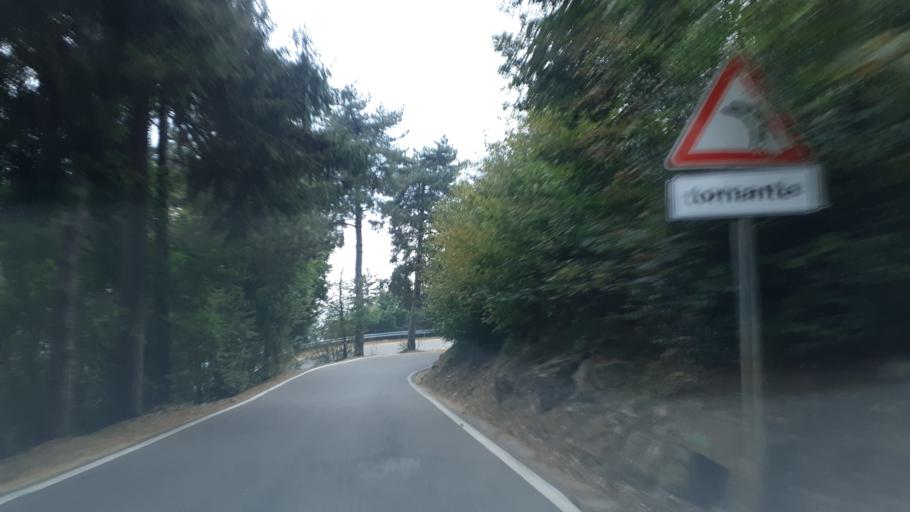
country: IT
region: Lombardy
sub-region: Provincia di Lecco
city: Ballabio
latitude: 45.8944
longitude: 9.4066
